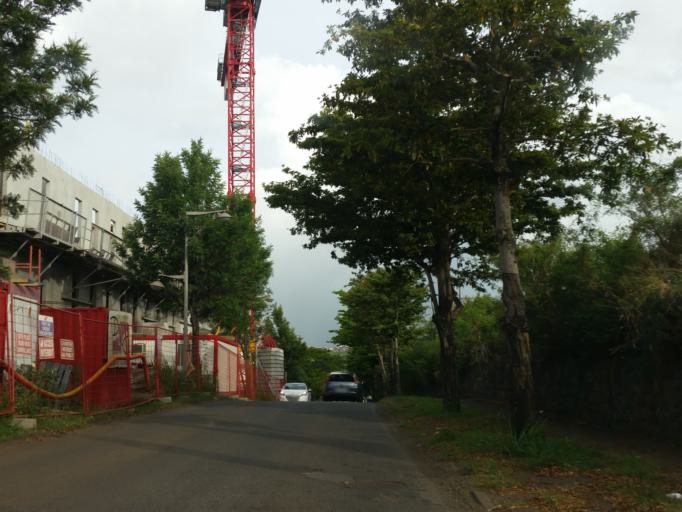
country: RE
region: Reunion
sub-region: Reunion
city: Sainte-Marie
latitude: -20.9073
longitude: 55.5023
